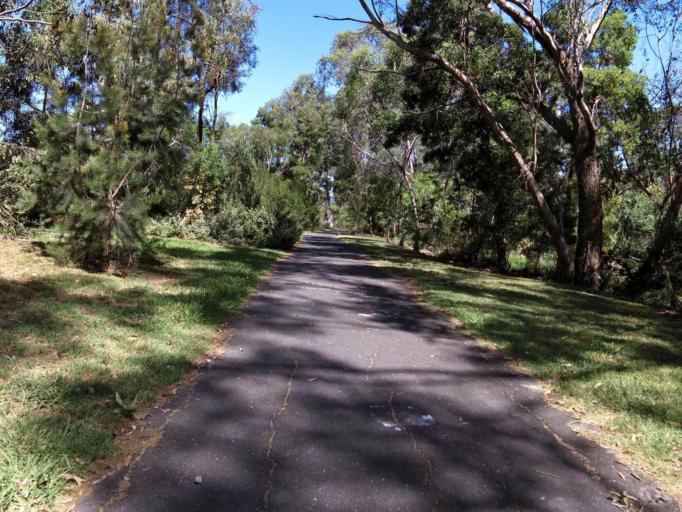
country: AU
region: Victoria
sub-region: Maroondah
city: Croydon North
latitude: -37.7826
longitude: 145.3068
